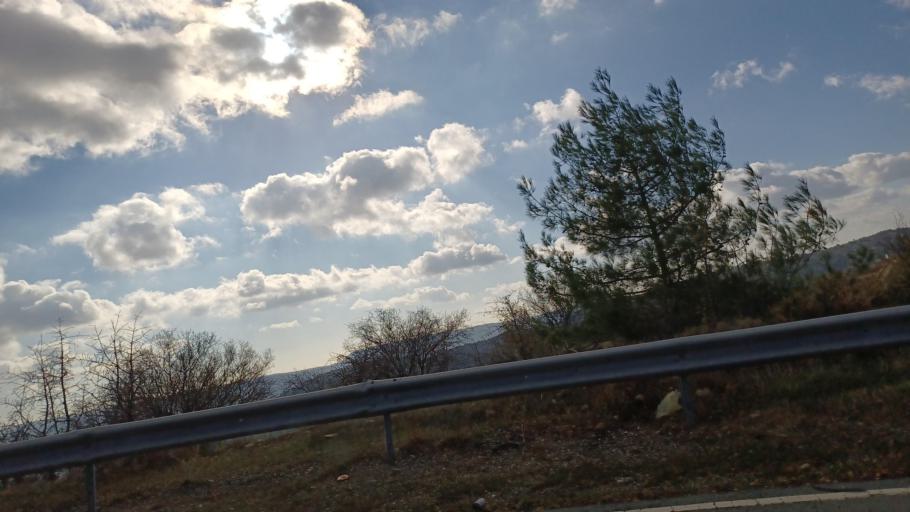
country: CY
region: Limassol
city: Pachna
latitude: 34.8480
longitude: 32.6937
